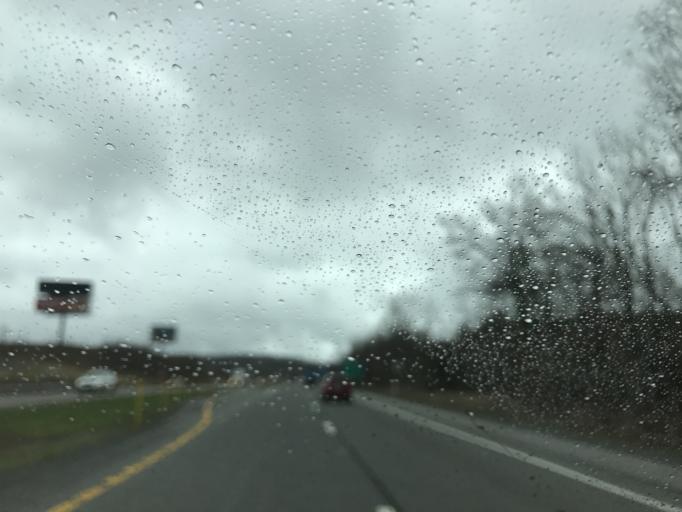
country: US
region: West Virginia
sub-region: Raleigh County
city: Bradley
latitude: 37.8656
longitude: -81.1881
